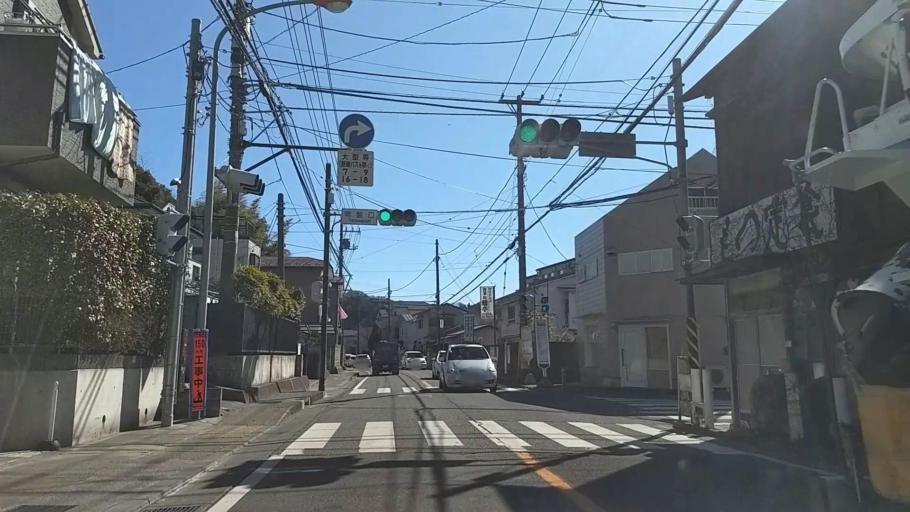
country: JP
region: Kanagawa
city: Kamakura
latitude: 35.3234
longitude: 139.5252
